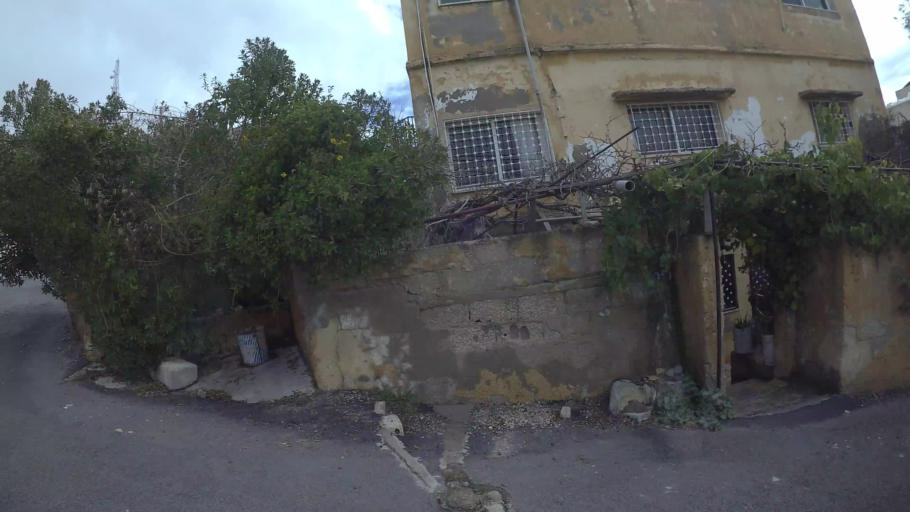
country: JO
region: Amman
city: Al Jubayhah
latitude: 32.0047
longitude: 35.8409
